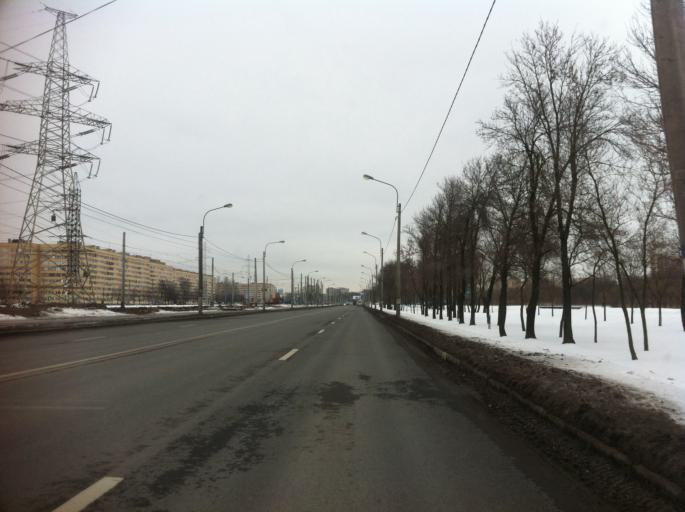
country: RU
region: St.-Petersburg
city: Uritsk
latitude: 59.8457
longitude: 30.1925
